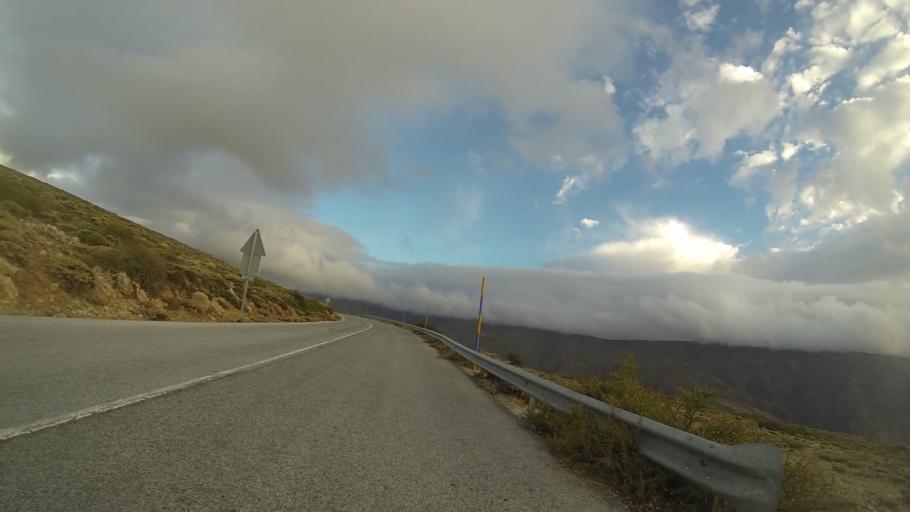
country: ES
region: Andalusia
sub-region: Provincia de Granada
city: Guejar-Sierra
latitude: 37.1178
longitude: -3.4309
